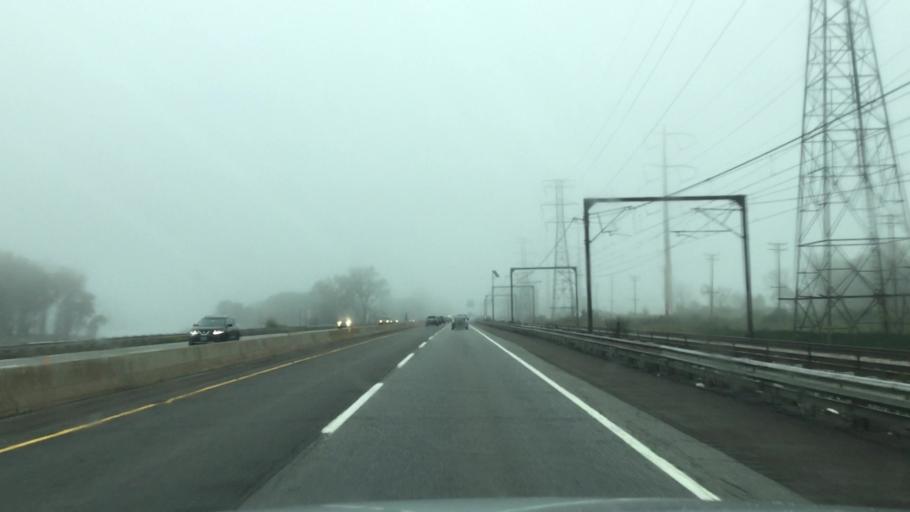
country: US
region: Indiana
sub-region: Lake County
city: East Chicago
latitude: 41.6105
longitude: -87.4494
